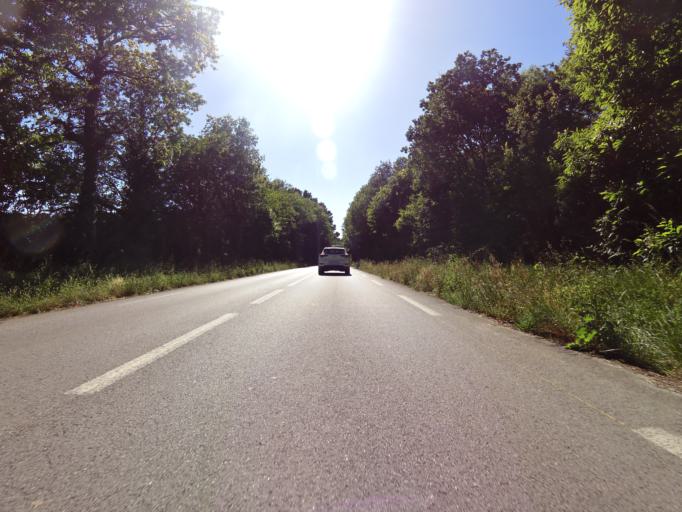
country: FR
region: Brittany
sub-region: Departement du Morbihan
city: Penestin
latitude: 47.4784
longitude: -2.4439
